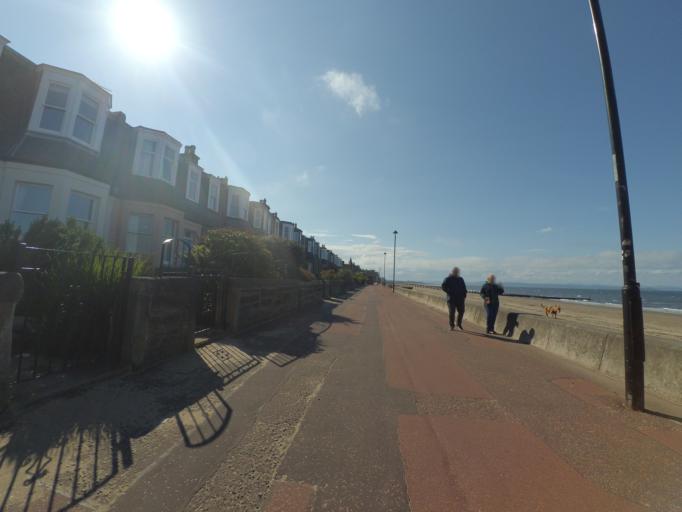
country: GB
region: Scotland
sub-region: East Lothian
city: Musselburgh
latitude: 55.9497
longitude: -3.0972
